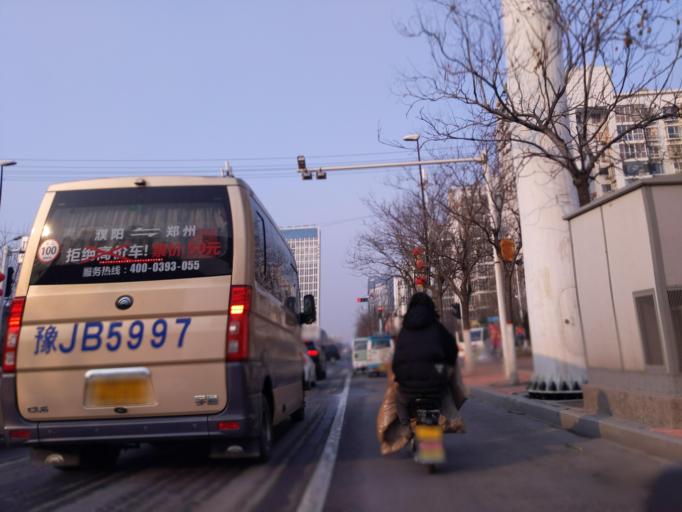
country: CN
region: Henan Sheng
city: Zhongyuanlu
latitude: 35.7636
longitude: 115.0572
